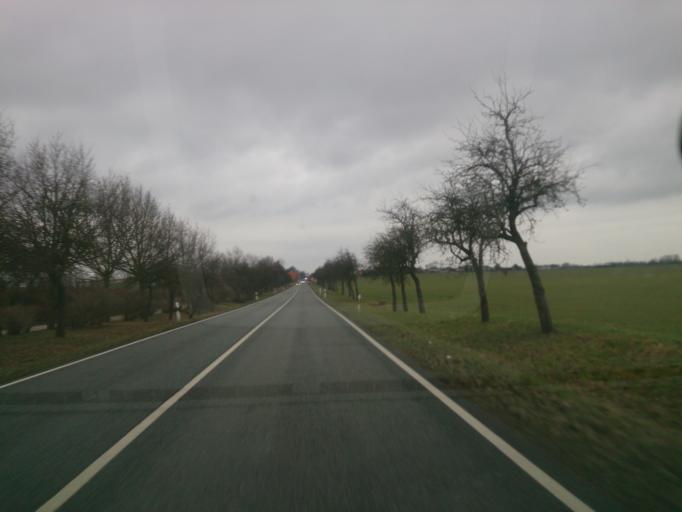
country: DE
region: Mecklenburg-Vorpommern
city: Wackerow
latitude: 53.7167
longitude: 12.9158
